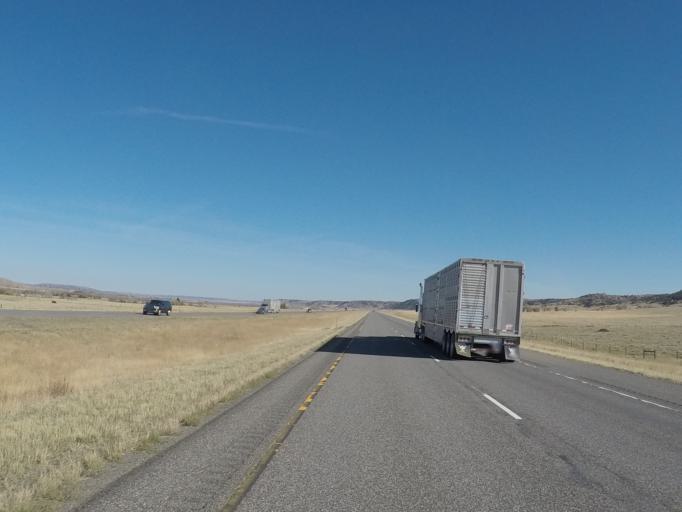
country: US
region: Montana
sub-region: Sweet Grass County
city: Big Timber
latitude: 45.7524
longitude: -110.1514
